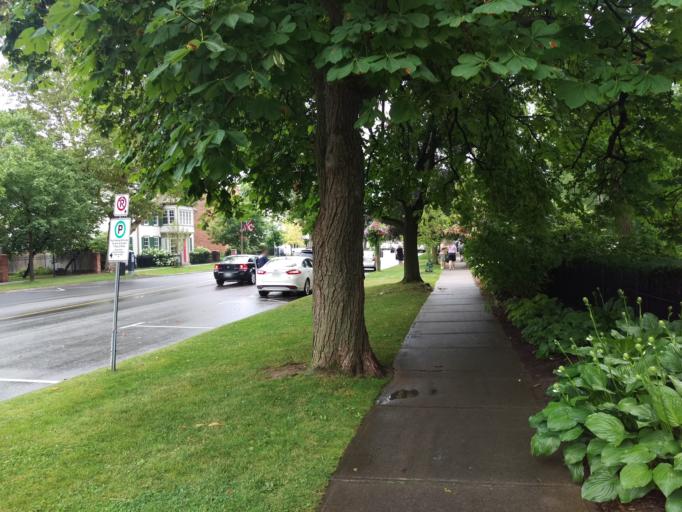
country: US
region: New York
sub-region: Niagara County
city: Youngstown
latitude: 43.2577
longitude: -79.0769
